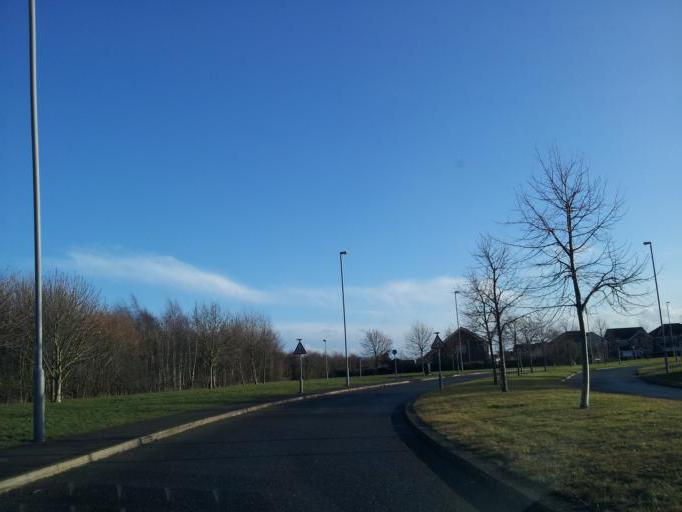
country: GB
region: England
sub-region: Nottinghamshire
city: Newark on Trent
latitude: 53.0770
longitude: -0.7718
